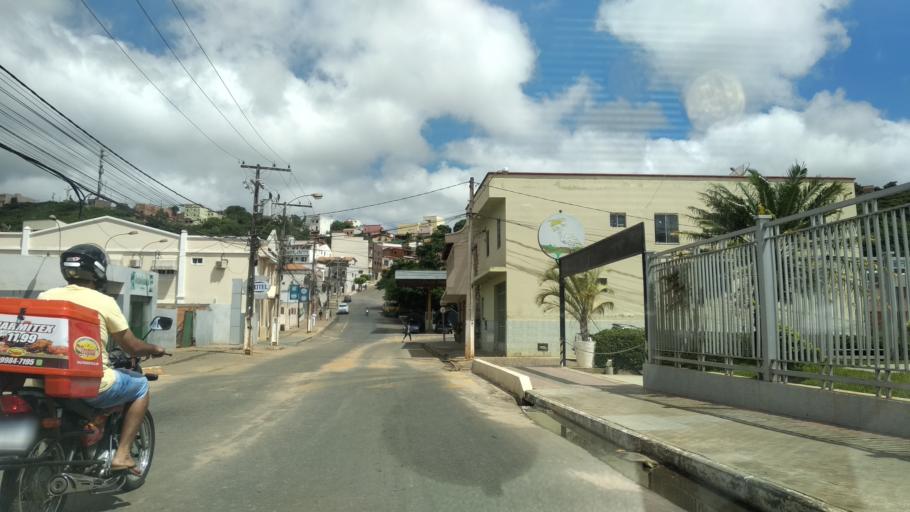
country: BR
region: Bahia
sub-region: Caetite
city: Caetite
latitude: -14.0666
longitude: -42.4846
